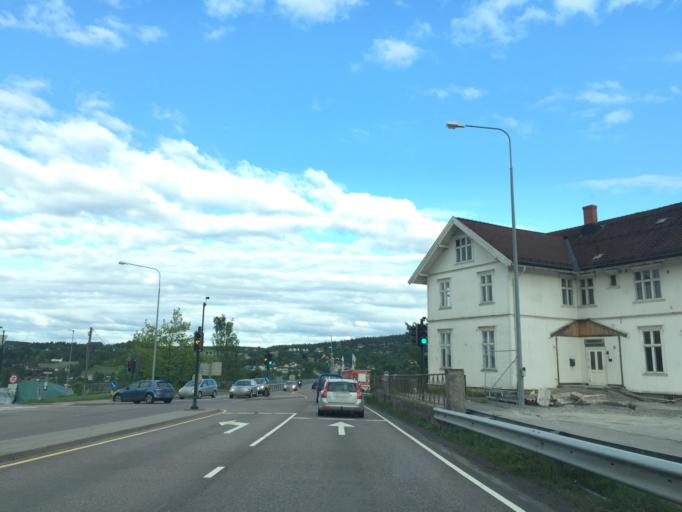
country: NO
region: Akershus
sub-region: Fet
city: Fetsund
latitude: 59.9247
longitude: 11.1563
